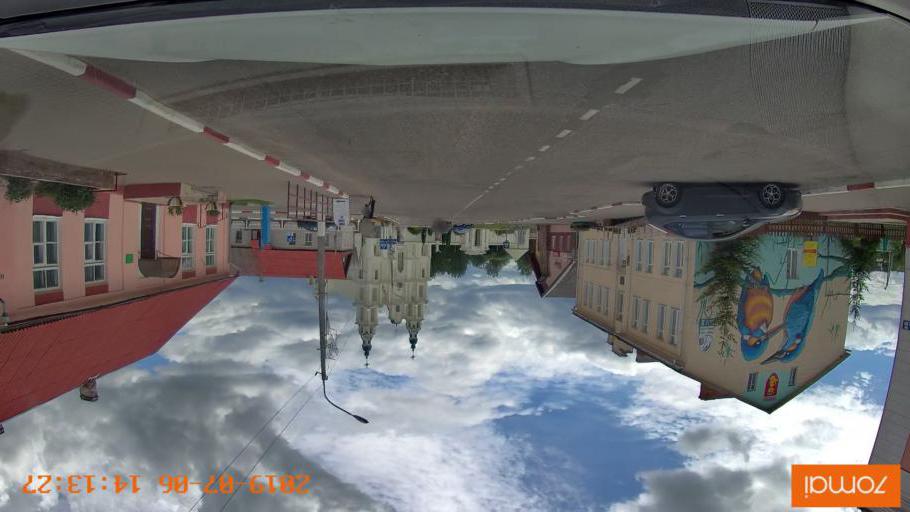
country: BY
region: Minsk
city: Ivyanyets
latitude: 53.8905
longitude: 26.7393
